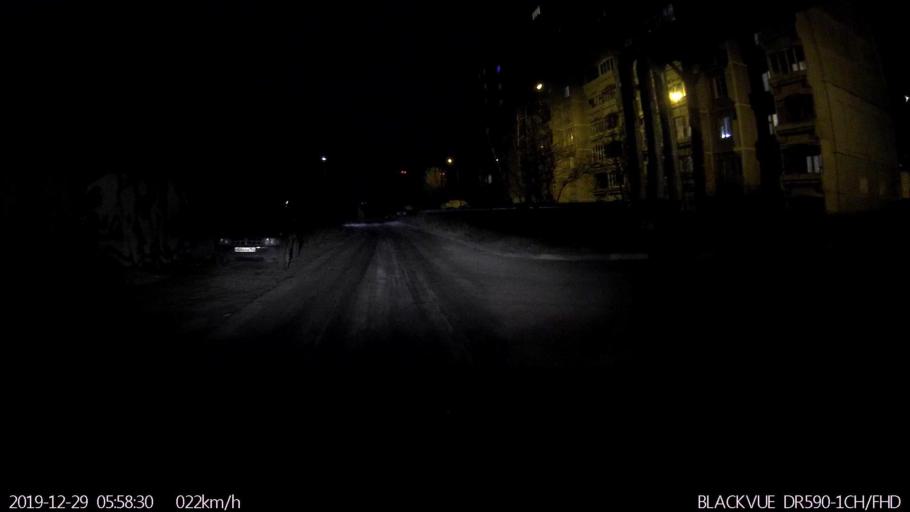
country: RU
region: Nizjnij Novgorod
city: Gorbatovka
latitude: 56.2266
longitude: 43.8227
